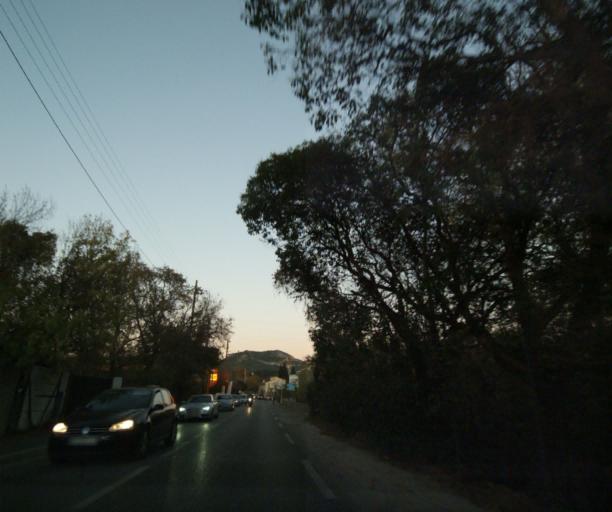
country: FR
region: Provence-Alpes-Cote d'Azur
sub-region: Departement des Bouches-du-Rhone
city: La Penne-sur-Huveaune
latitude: 43.2986
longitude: 5.4995
